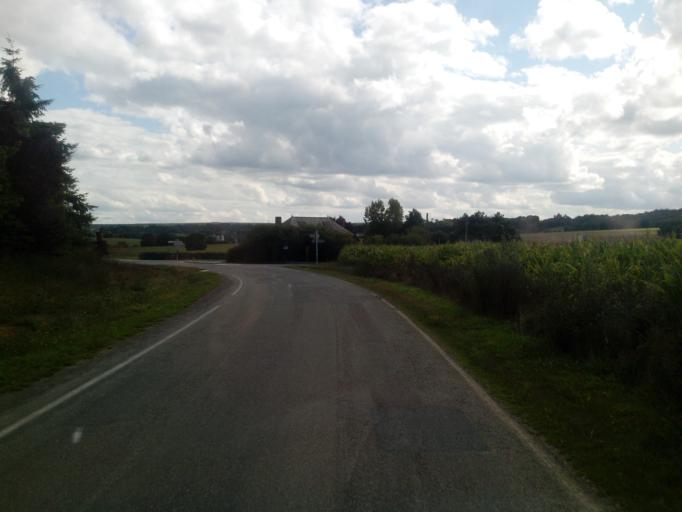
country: FR
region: Brittany
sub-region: Departement d'Ille-et-Vilaine
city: Boisgervilly
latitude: 48.0976
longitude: -2.1176
